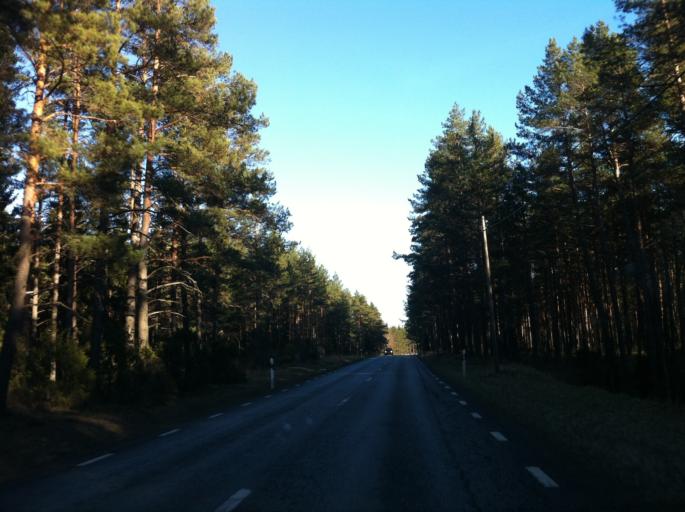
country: SE
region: Uppsala
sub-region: Osthammars Kommun
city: Anneberg
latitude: 60.1771
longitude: 18.3996
